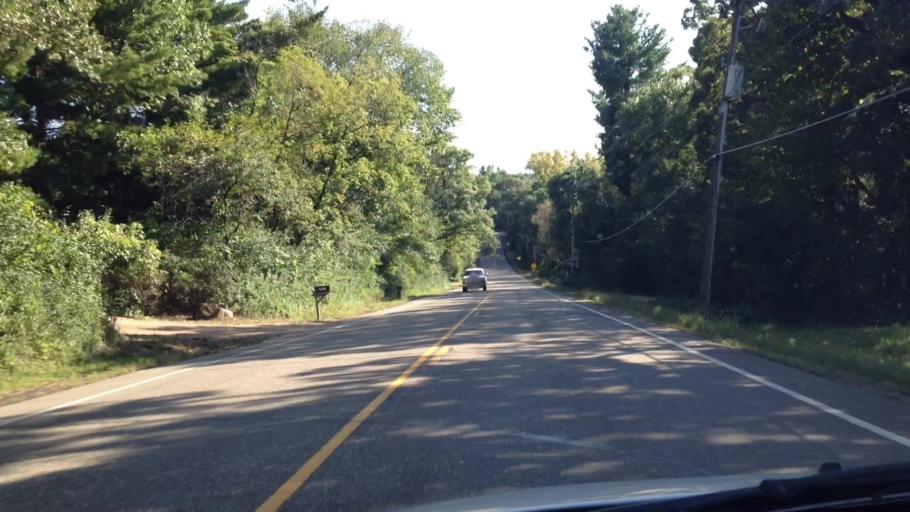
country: US
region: Minnesota
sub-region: Washington County
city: Stillwater
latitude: 45.0864
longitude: -92.8130
